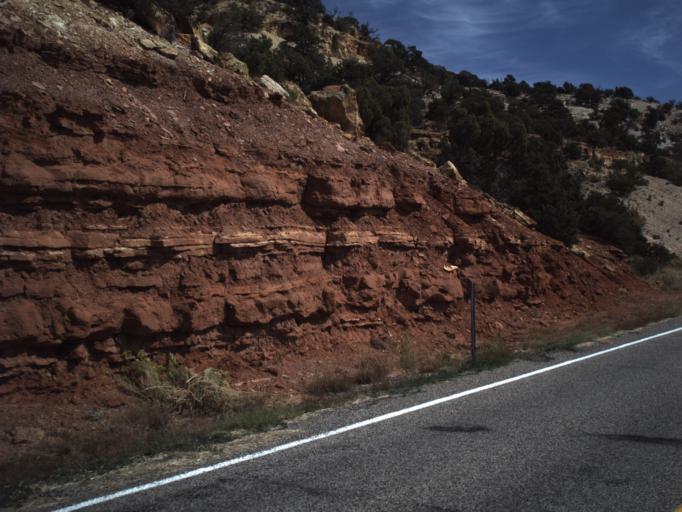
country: US
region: Utah
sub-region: Wayne County
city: Loa
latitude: 37.8928
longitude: -111.4540
